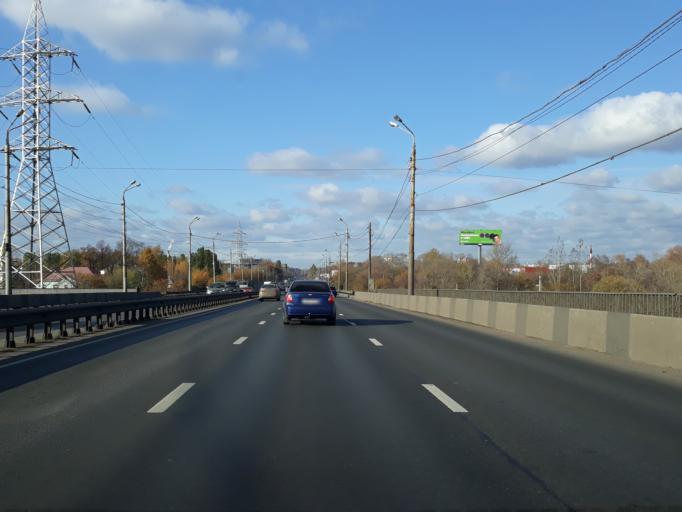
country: RU
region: Nizjnij Novgorod
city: Nizhniy Novgorod
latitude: 56.2553
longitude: 43.9383
